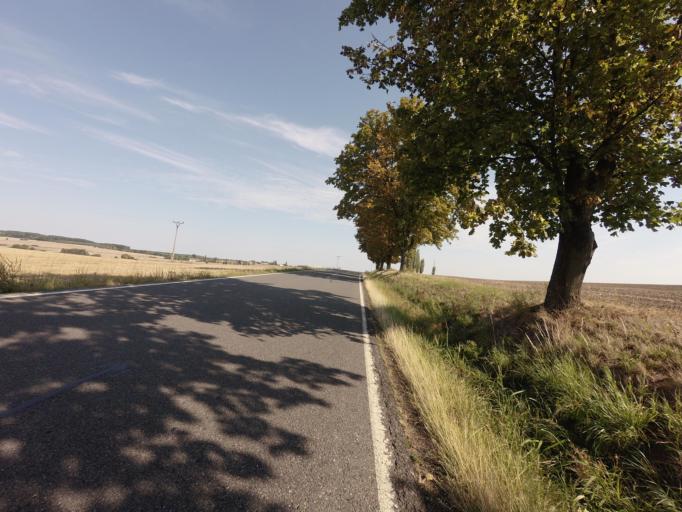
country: CZ
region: Jihocesky
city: Bernartice
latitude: 49.3301
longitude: 14.3599
